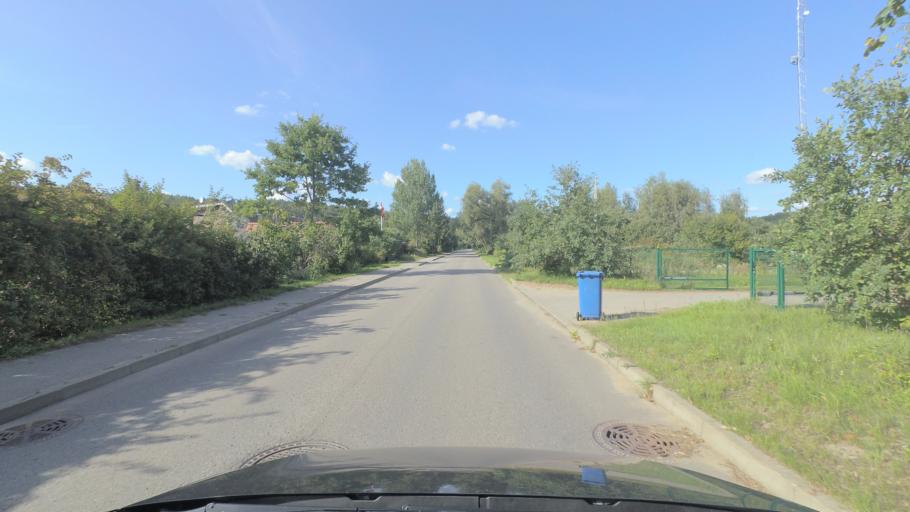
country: LT
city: Nemencine
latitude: 54.8388
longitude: 25.3708
